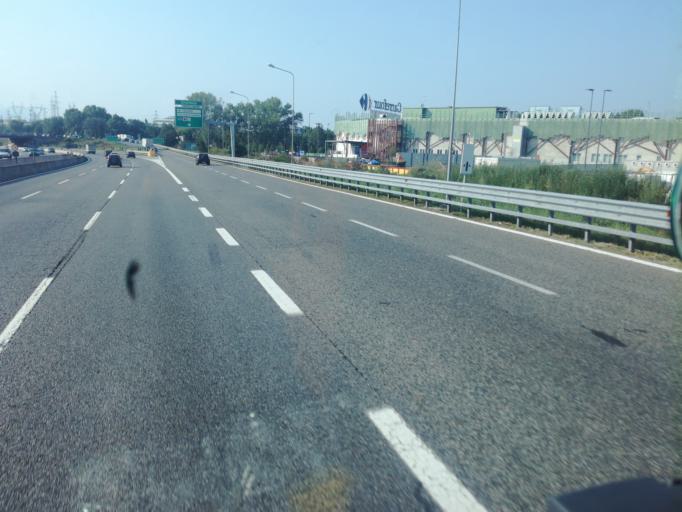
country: IT
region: Piedmont
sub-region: Provincia di Torino
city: Nichelino
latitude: 45.0053
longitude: 7.6215
